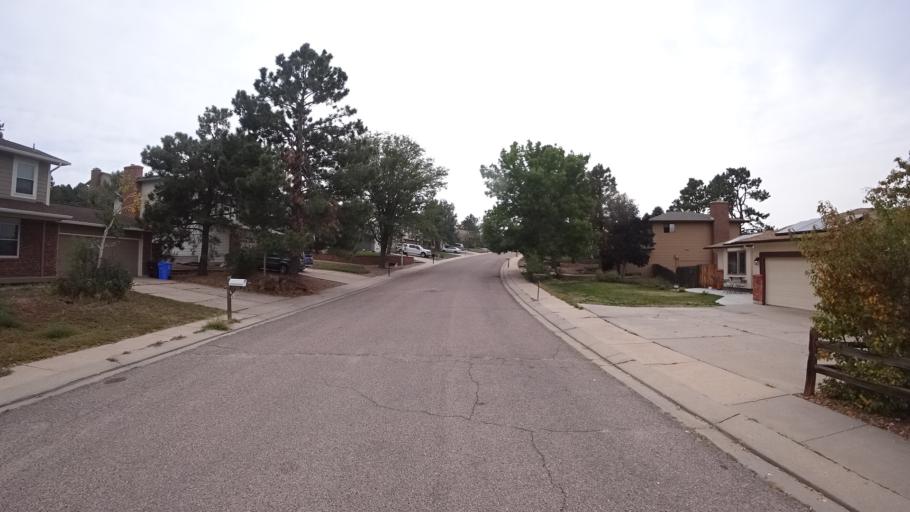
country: US
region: Colorado
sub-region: El Paso County
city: Cimarron Hills
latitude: 38.9005
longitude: -104.7261
